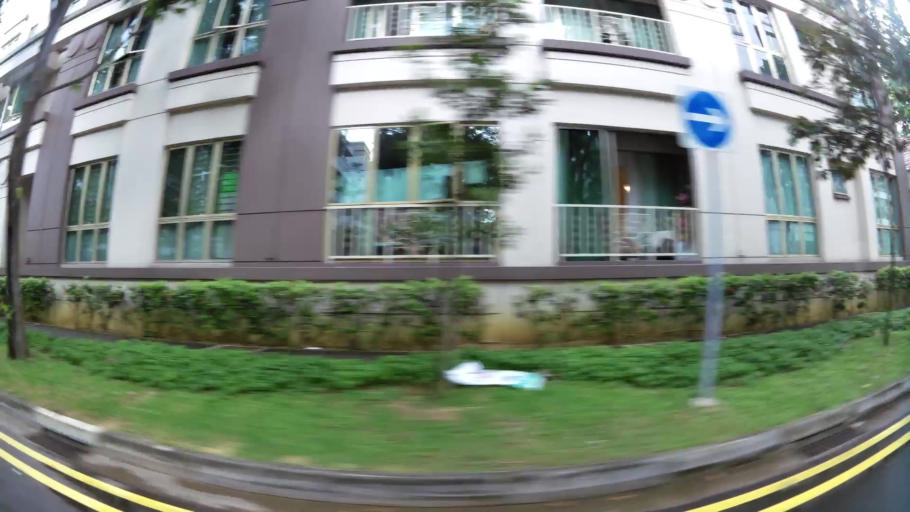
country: SG
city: Singapore
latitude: 1.3160
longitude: 103.8526
